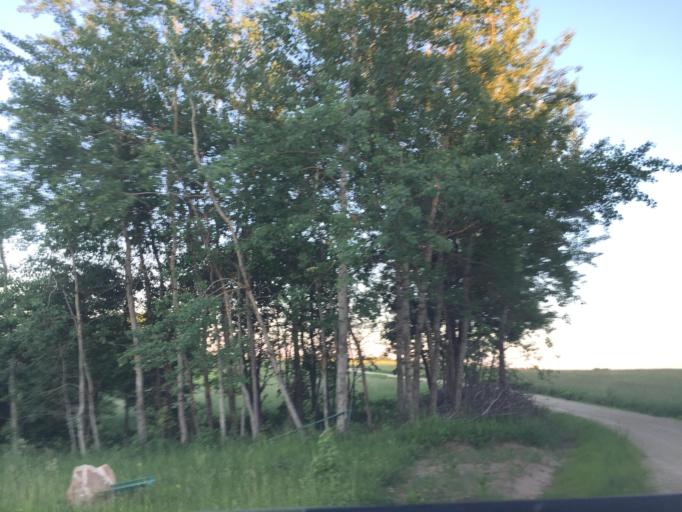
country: LV
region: Rezekne
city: Rezekne
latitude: 56.3623
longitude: 27.4123
